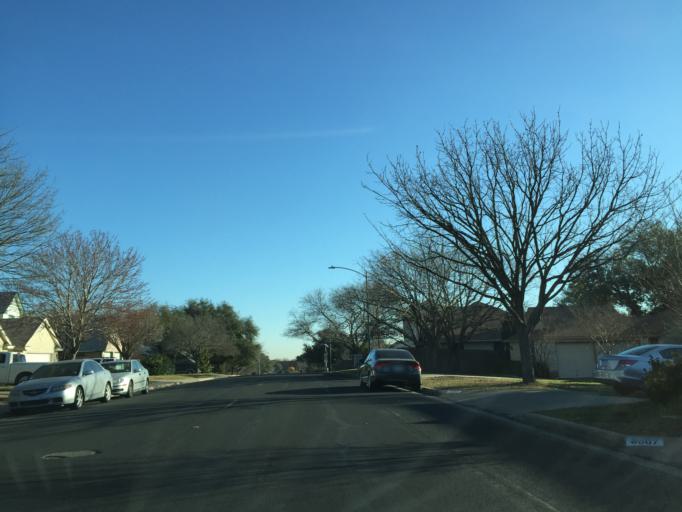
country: US
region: Texas
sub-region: Williamson County
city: Jollyville
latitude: 30.4442
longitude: -97.7677
